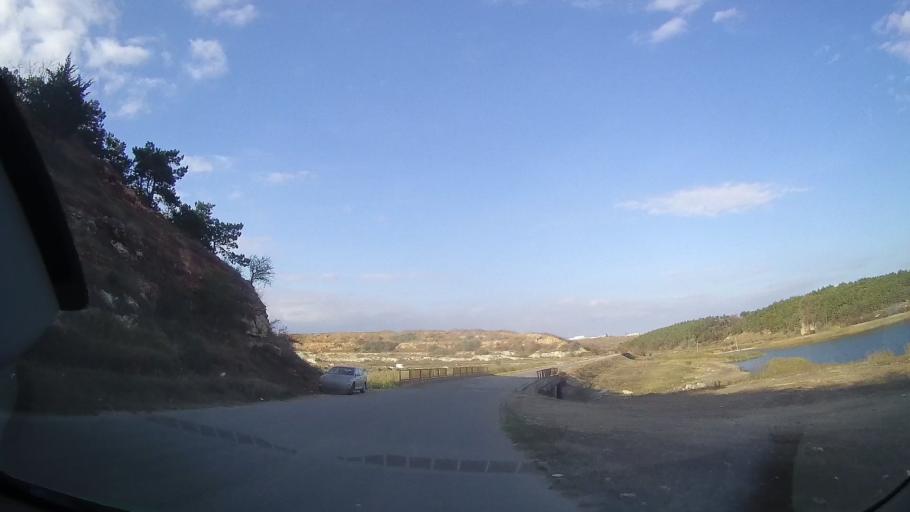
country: RO
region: Constanta
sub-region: Comuna Limanu
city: Limanu
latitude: 43.8120
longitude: 28.5169
